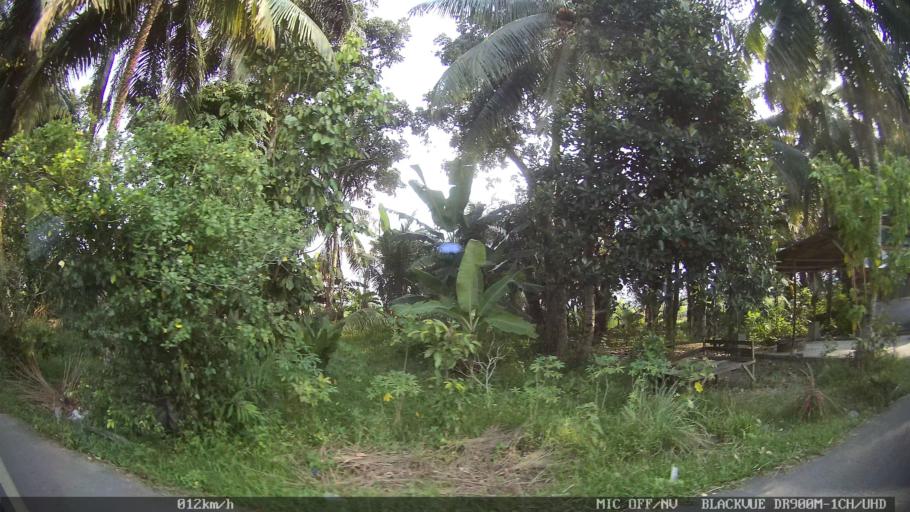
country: ID
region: North Sumatra
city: Binjai
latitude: 3.6029
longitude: 98.5050
